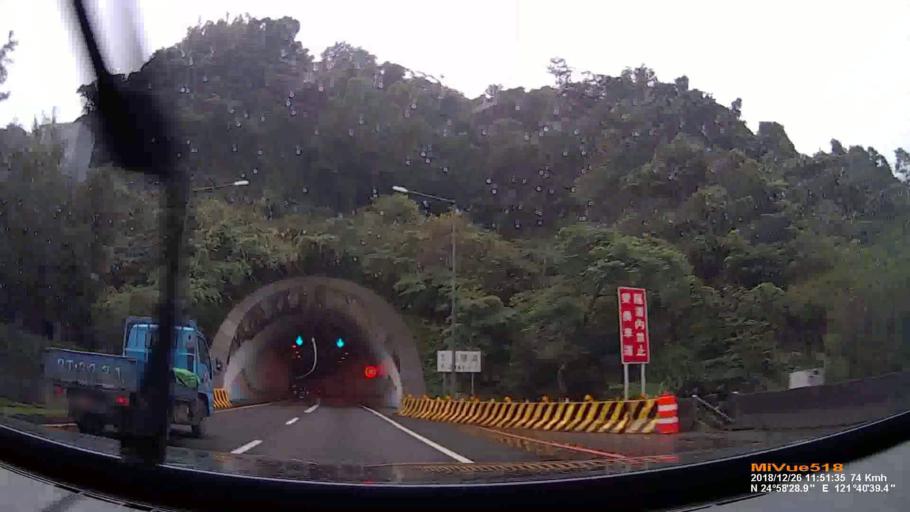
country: TW
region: Taipei
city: Taipei
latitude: 24.9739
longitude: 121.6780
